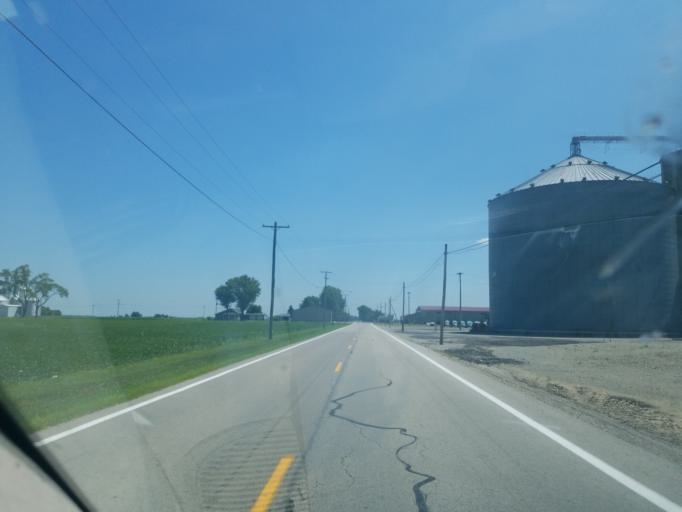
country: US
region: Ohio
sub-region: Allen County
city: Spencerville
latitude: 40.7426
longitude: -84.4784
